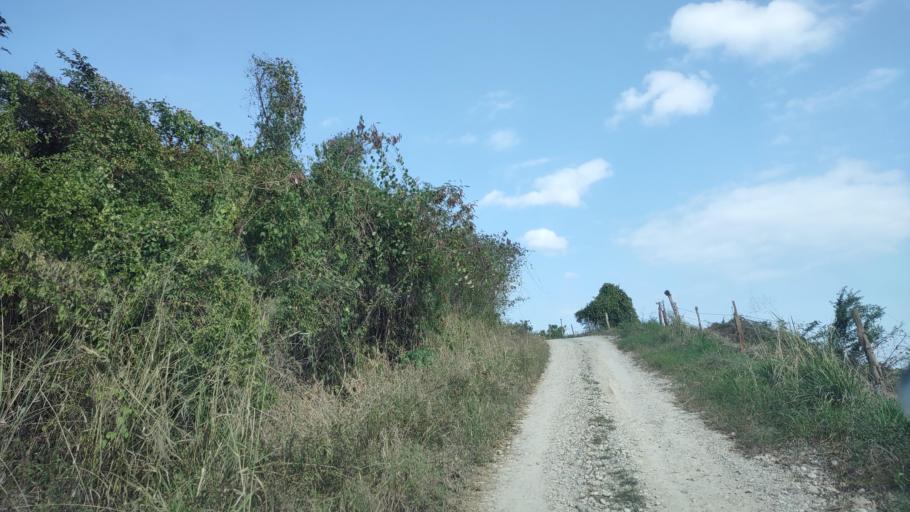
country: MX
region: Veracruz
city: Papantla de Olarte
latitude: 20.4575
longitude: -97.3969
